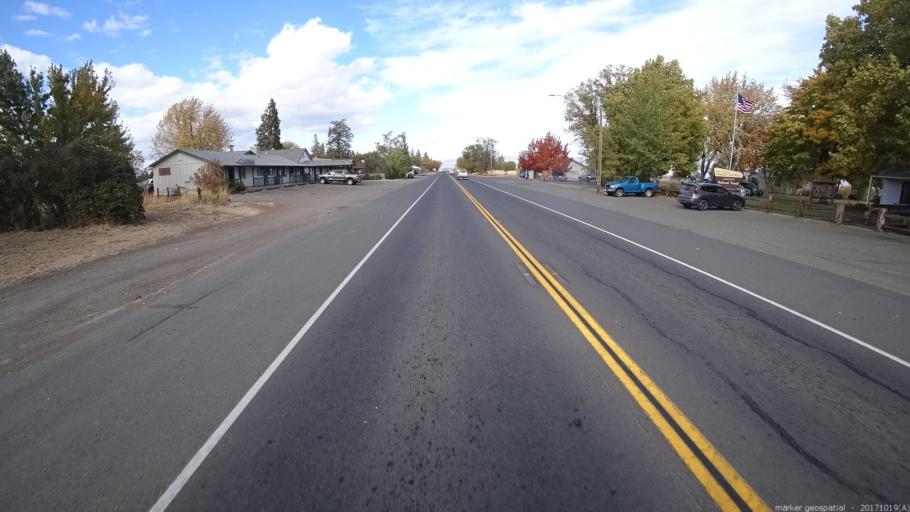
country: US
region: California
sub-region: Shasta County
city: Burney
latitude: 41.0082
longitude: -121.4362
